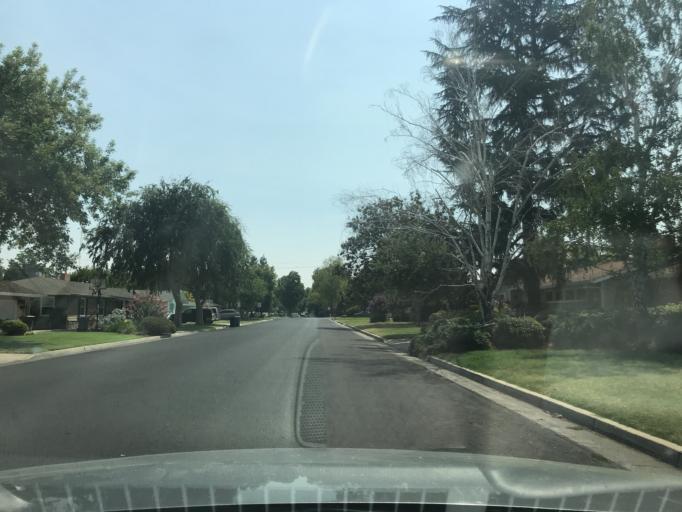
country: US
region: California
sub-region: Merced County
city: Merced
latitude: 37.3153
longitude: -120.4801
